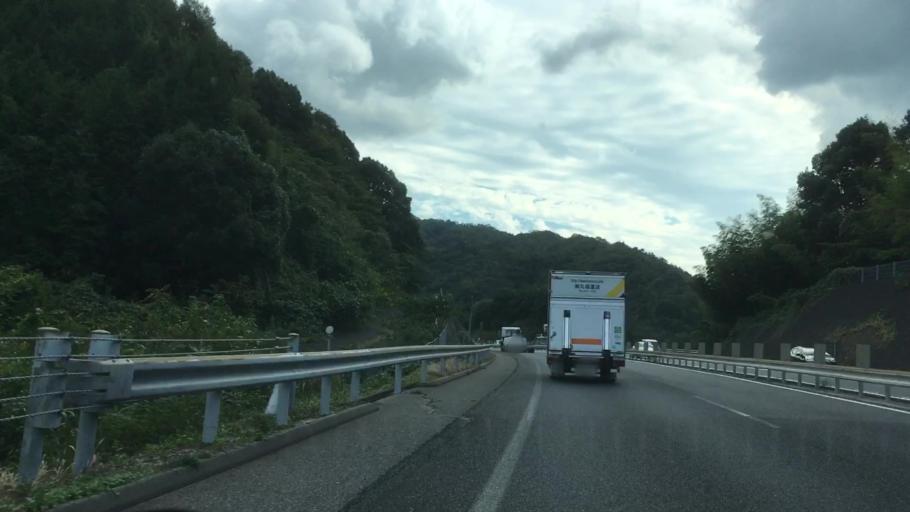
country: JP
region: Yamaguchi
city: Iwakuni
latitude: 34.1258
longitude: 132.1110
